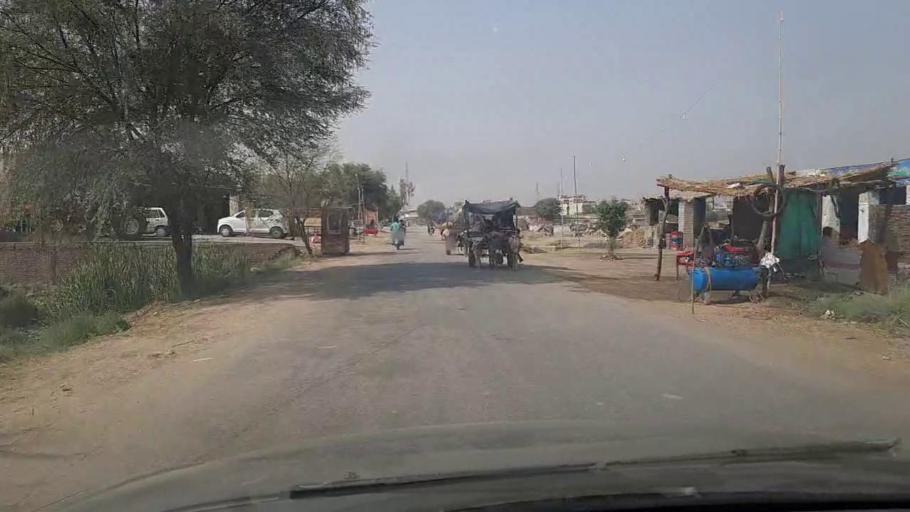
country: PK
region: Sindh
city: Mirpur Mathelo
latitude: 27.9196
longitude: 69.5244
